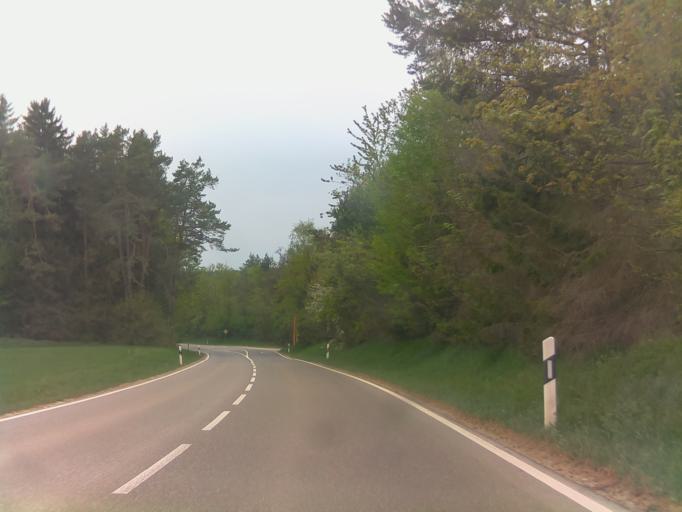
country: DE
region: Baden-Wuerttemberg
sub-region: Freiburg Region
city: Niedereschach
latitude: 48.1561
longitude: 8.5570
